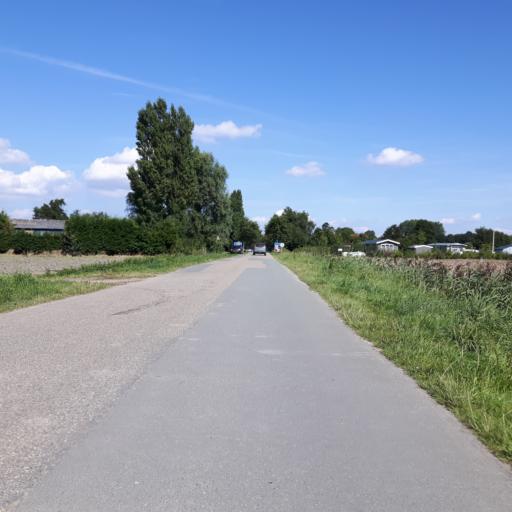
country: NL
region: Zeeland
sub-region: Schouwen-Duiveland
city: Bruinisse
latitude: 51.6213
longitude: 3.9847
